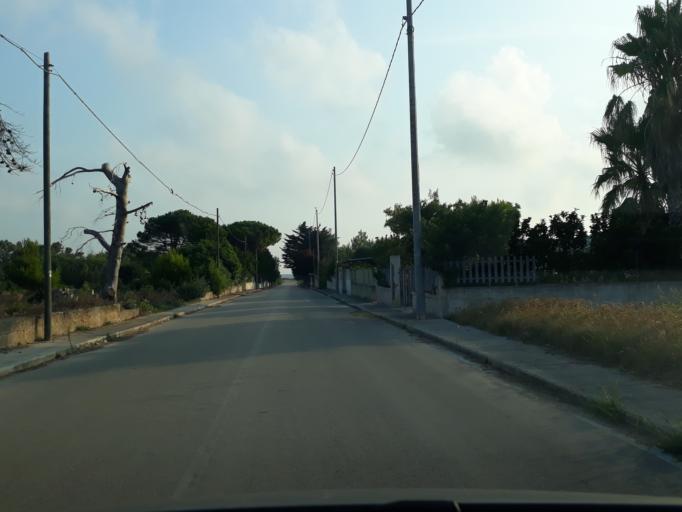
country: IT
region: Apulia
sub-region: Provincia di Brindisi
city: Carovigno
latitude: 40.7496
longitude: 17.7153
